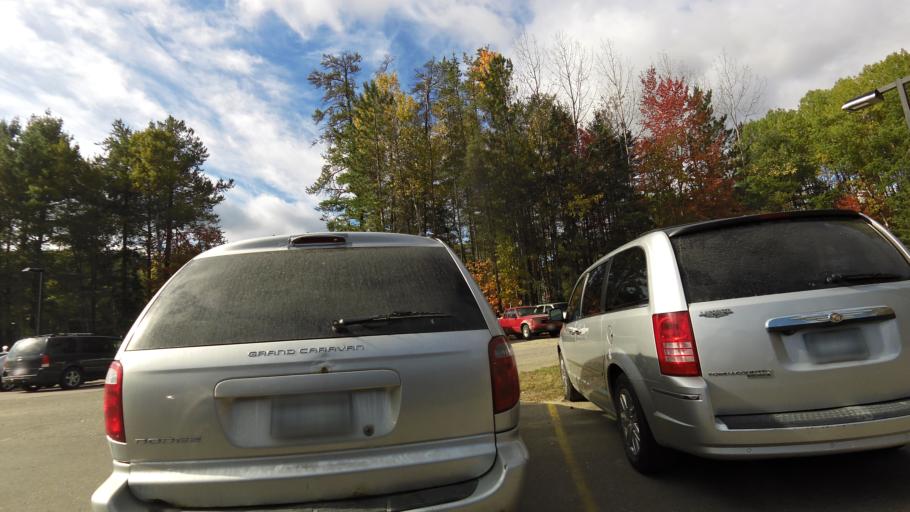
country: CA
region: Ontario
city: Deep River
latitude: 46.0911
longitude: -77.4757
